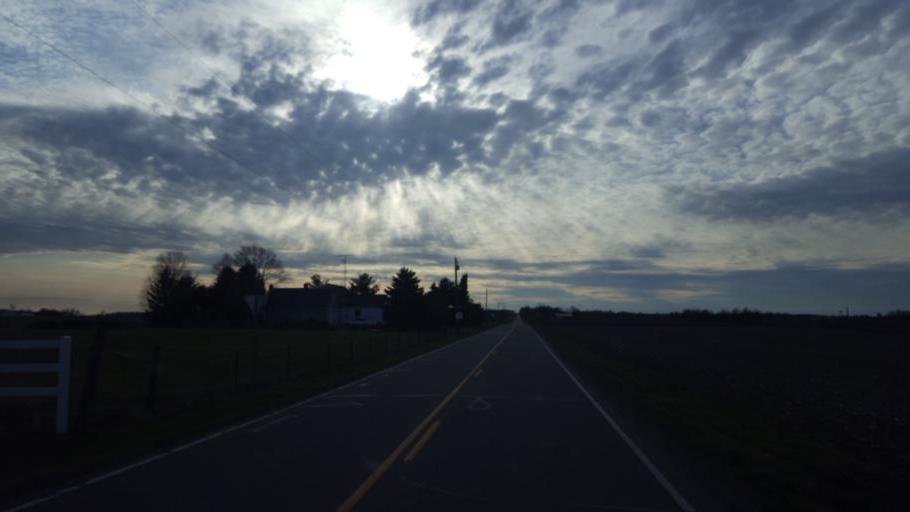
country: US
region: Ohio
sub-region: Crawford County
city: Bucyrus
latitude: 40.7984
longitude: -82.9024
